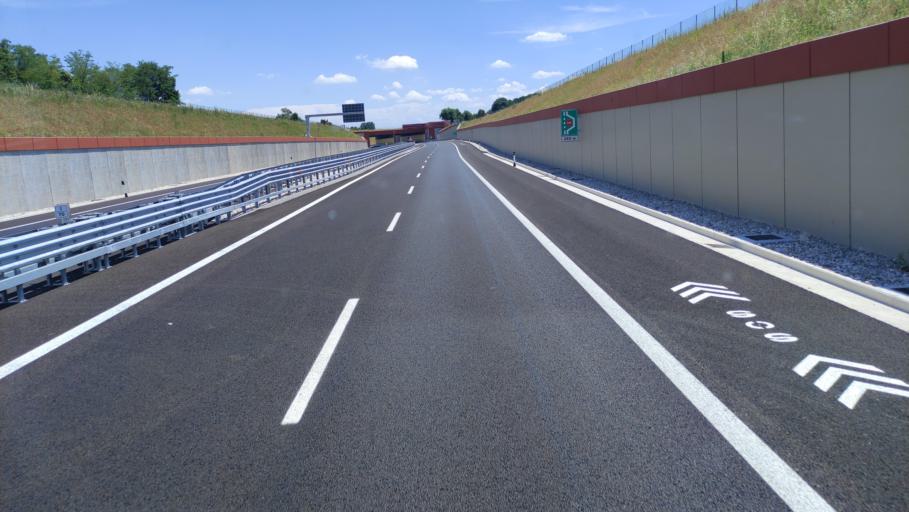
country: IT
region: Veneto
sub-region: Provincia di Treviso
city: Fanzolo
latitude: 45.7288
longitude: 11.9858
